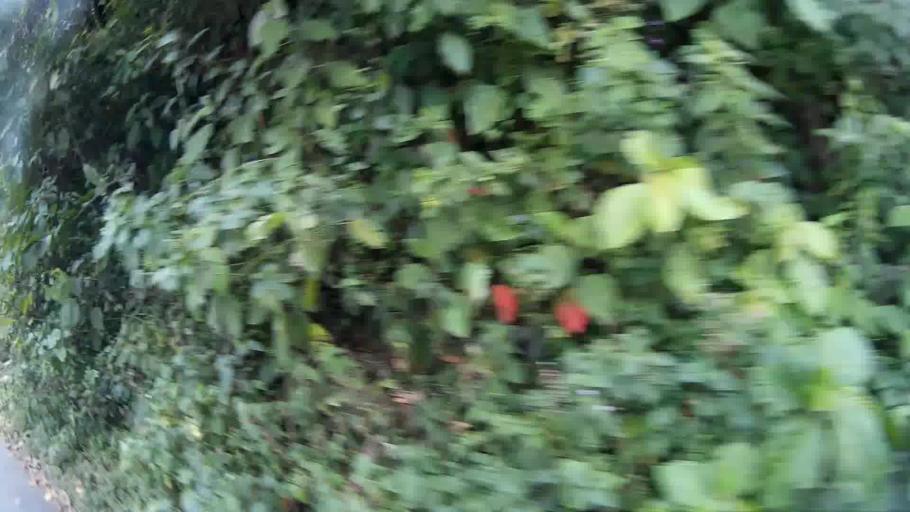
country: CO
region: Risaralda
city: Marsella
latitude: 4.8812
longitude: -75.7591
